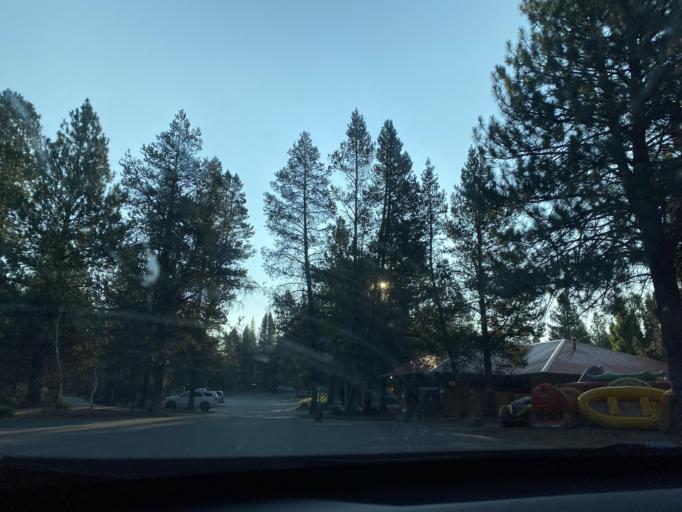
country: US
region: Oregon
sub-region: Deschutes County
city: Sunriver
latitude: 43.8747
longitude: -121.4372
